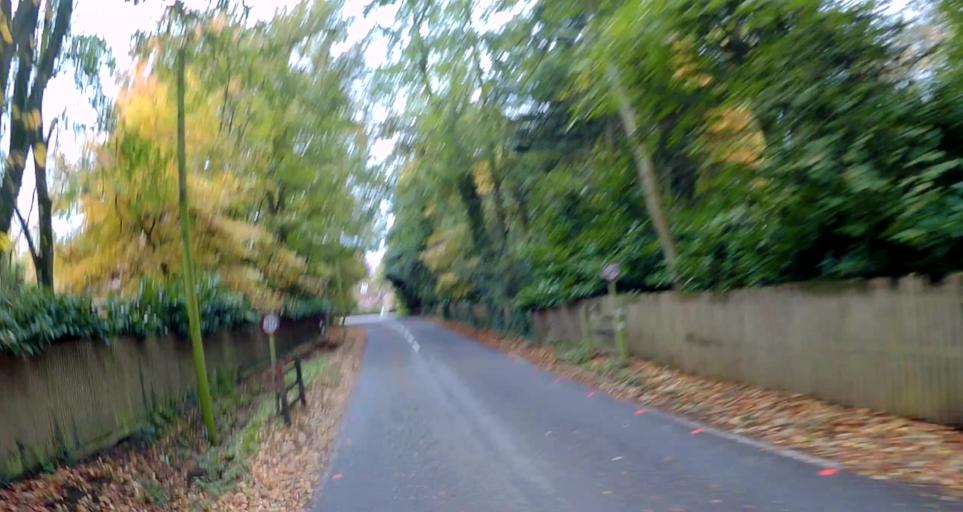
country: GB
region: England
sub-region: Hampshire
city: Basingstoke
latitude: 51.1695
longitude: -1.1358
